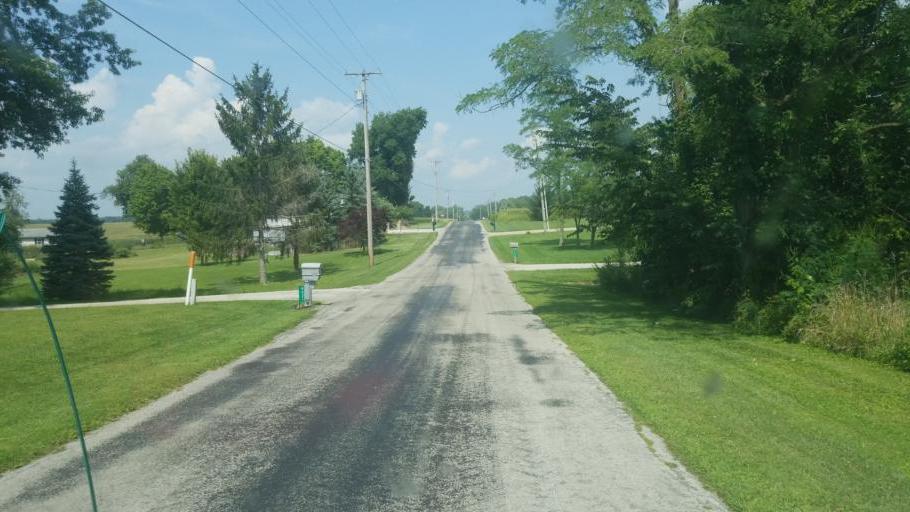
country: US
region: Ohio
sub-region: Richland County
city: Shelby
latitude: 40.8783
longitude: -82.5956
